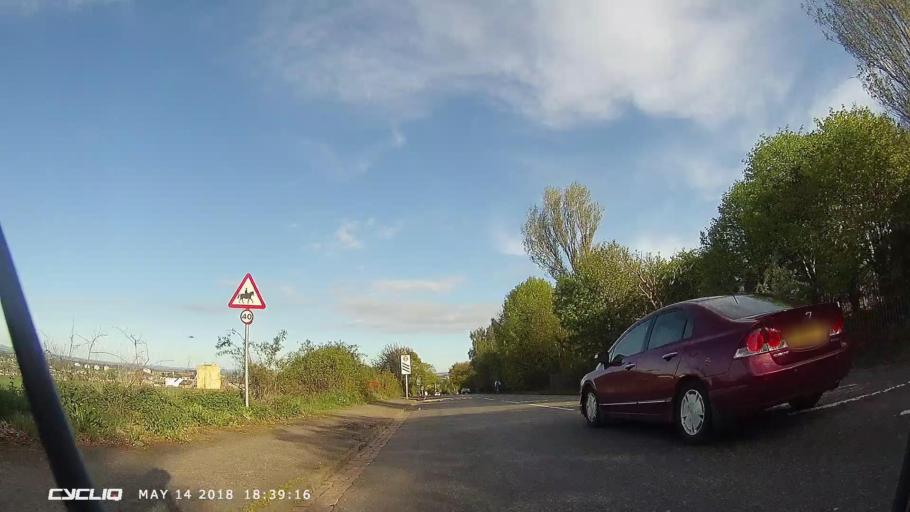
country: GB
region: Scotland
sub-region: Edinburgh
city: Edinburgh
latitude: 55.9149
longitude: -3.1810
